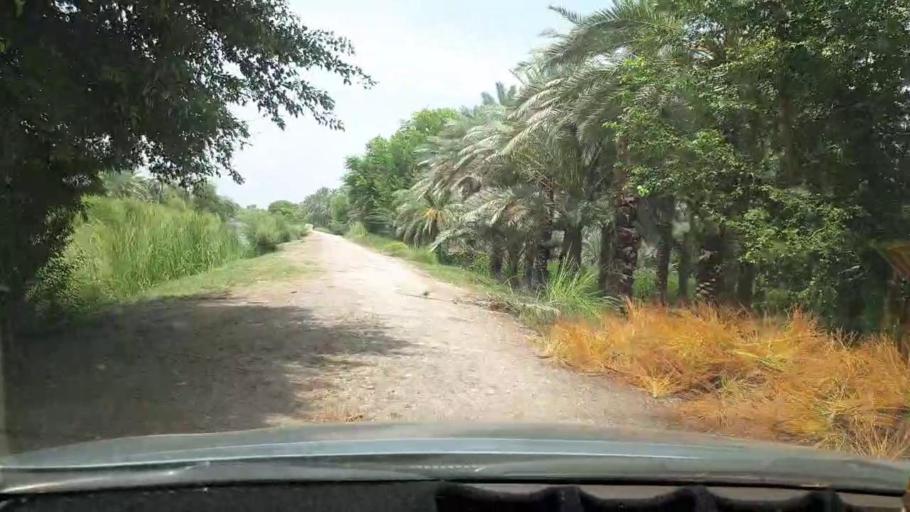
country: PK
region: Sindh
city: Khairpur
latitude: 27.4610
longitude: 68.8034
